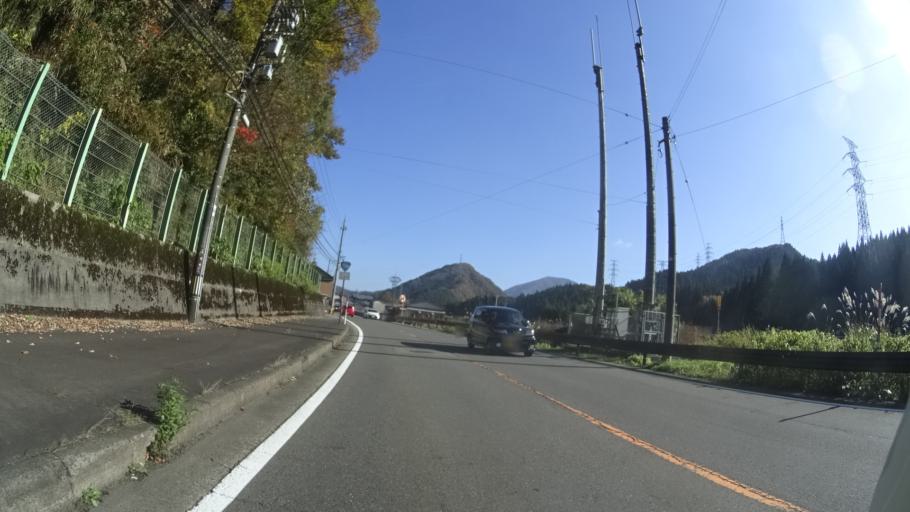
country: JP
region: Fukui
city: Ono
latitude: 36.0015
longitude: 136.4060
